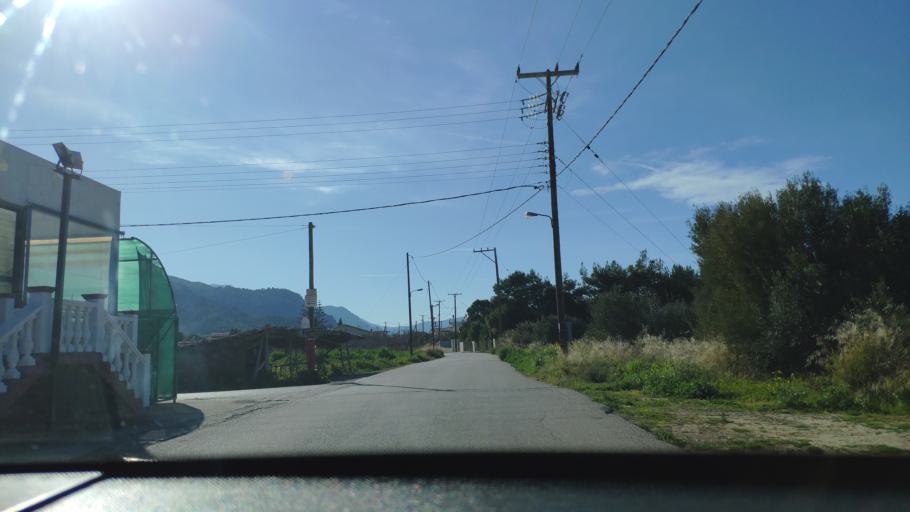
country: GR
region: Attica
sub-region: Nomarchia Dytikis Attikis
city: Kineta
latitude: 38.0709
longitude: 23.1563
